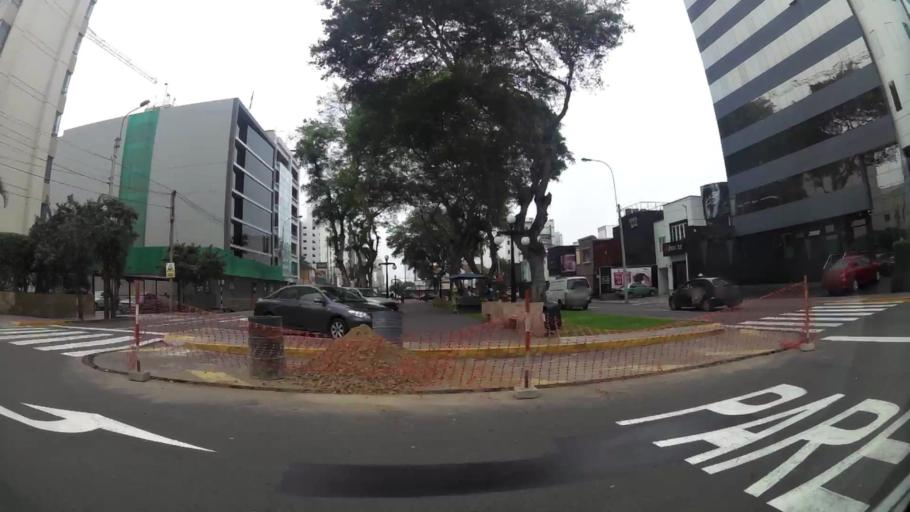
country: PE
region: Lima
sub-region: Lima
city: San Isidro
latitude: -12.1201
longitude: -77.0370
